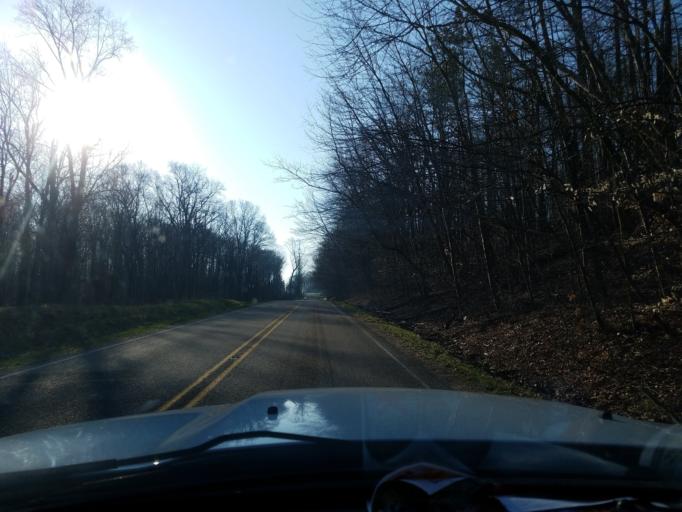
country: US
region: Indiana
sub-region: Owen County
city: Spencer
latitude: 39.3445
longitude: -86.9103
